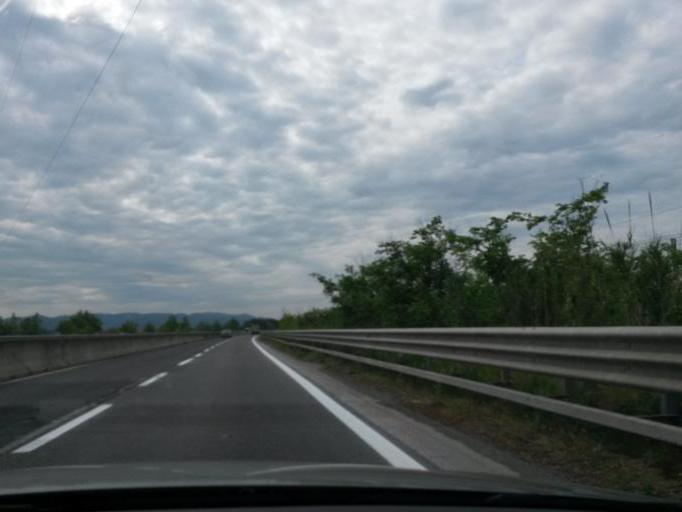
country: IT
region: Tuscany
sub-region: Provincia di Livorno
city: La California
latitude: 43.2244
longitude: 10.5598
